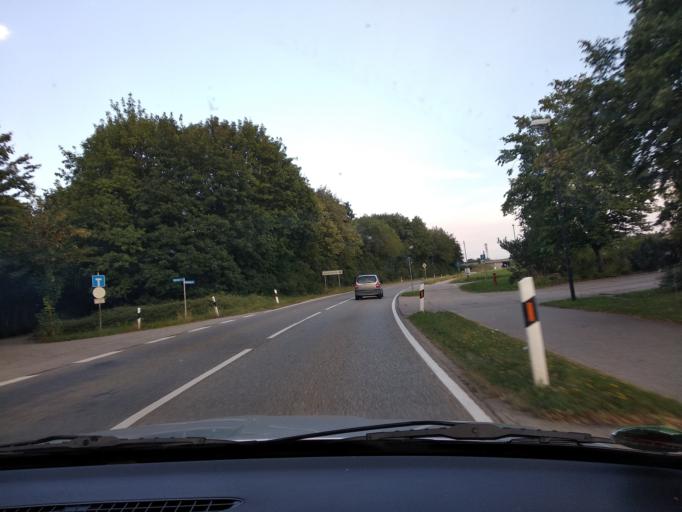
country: DE
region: Bavaria
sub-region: Upper Bavaria
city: Feldkirchen
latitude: 48.1454
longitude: 11.7504
